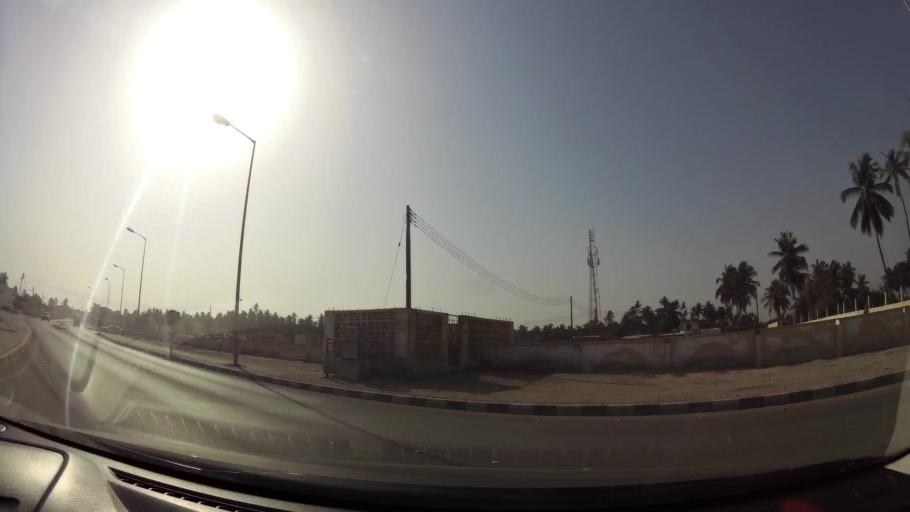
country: OM
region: Zufar
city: Salalah
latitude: 17.0029
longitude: 54.1124
